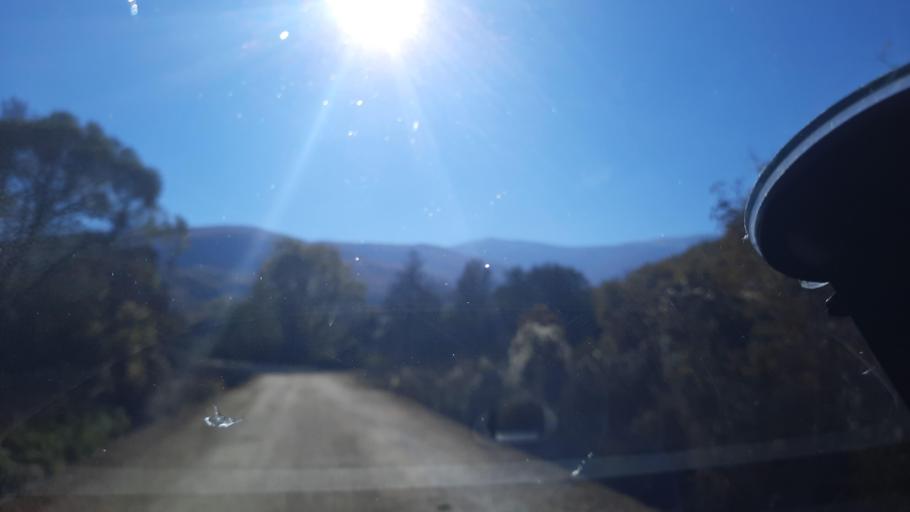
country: MK
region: Demir Hisar
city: Sopotnica
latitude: 41.2733
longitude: 21.0872
